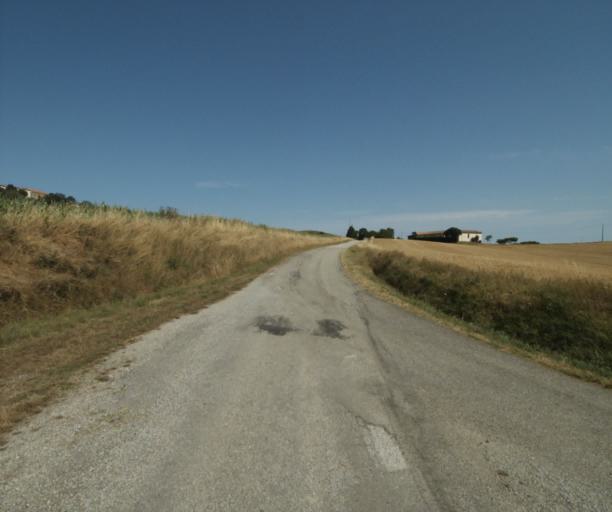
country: FR
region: Midi-Pyrenees
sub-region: Departement de la Haute-Garonne
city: Saint-Felix-Lauragais
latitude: 43.4475
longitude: 1.8829
